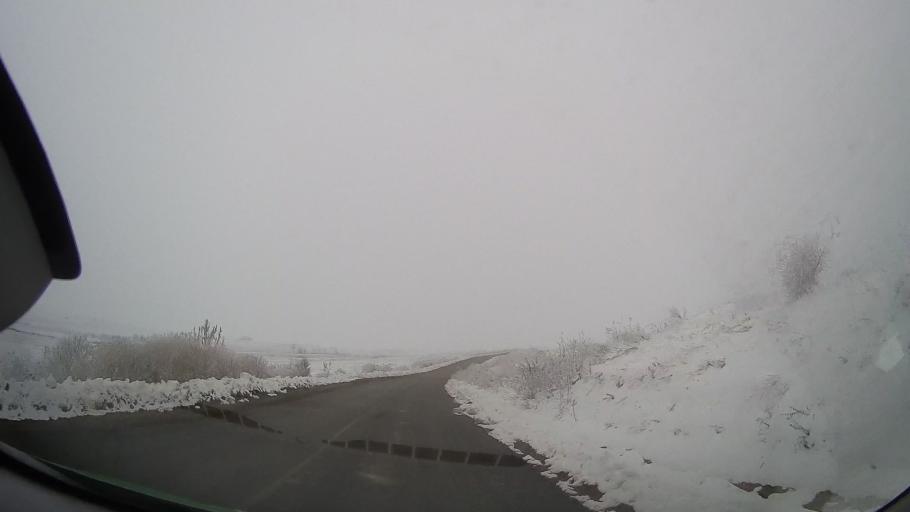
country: RO
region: Iasi
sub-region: Comuna Tansa
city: Suhulet
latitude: 46.8866
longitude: 27.2767
